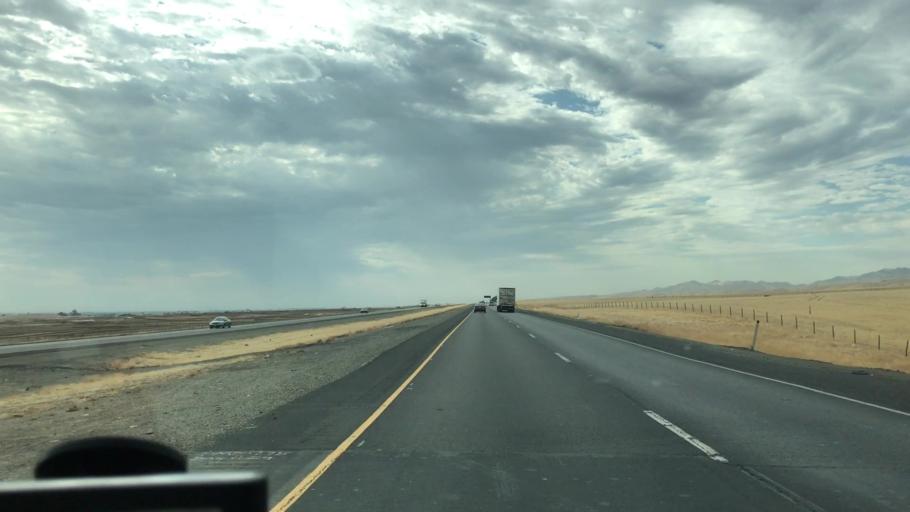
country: US
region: California
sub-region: San Joaquin County
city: Tracy
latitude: 37.6858
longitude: -121.4799
